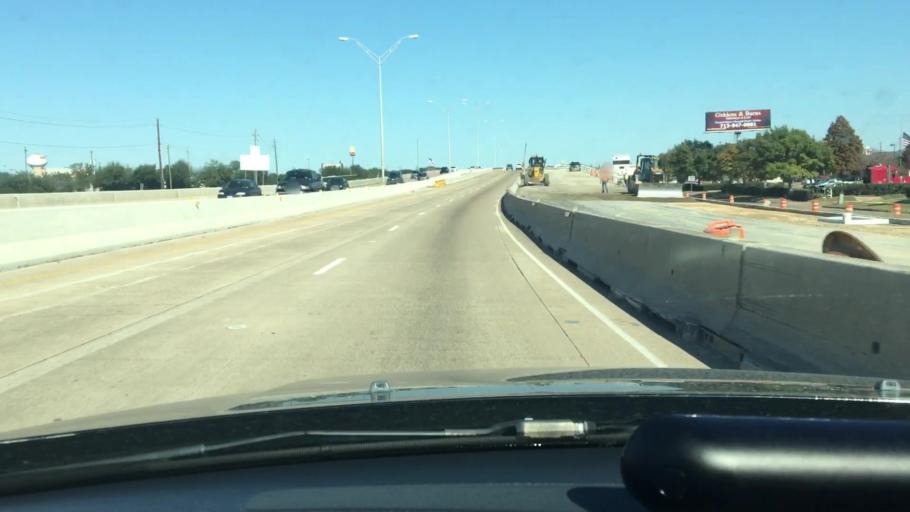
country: US
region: Texas
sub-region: Harris County
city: Deer Park
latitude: 29.6795
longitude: -95.1559
